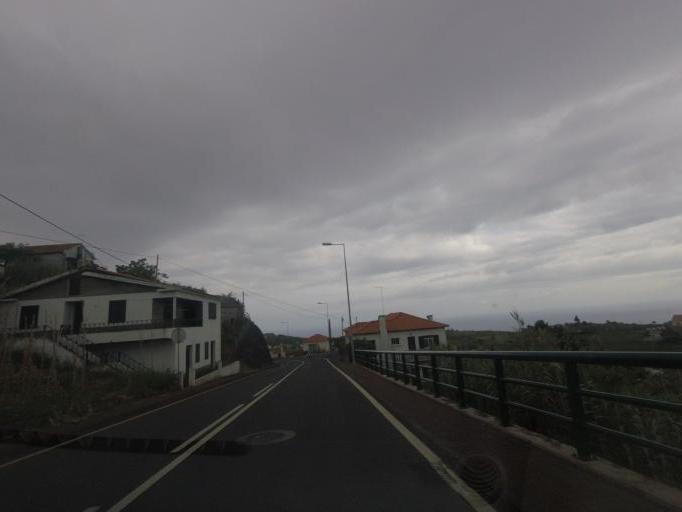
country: PT
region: Madeira
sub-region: Santana
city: Santana
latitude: 32.8205
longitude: -16.8880
